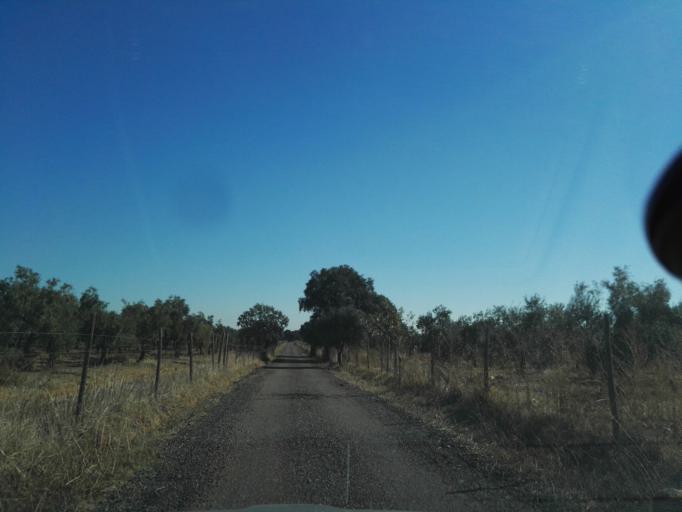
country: PT
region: Portalegre
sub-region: Elvas
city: Elvas
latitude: 38.9196
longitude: -7.1807
